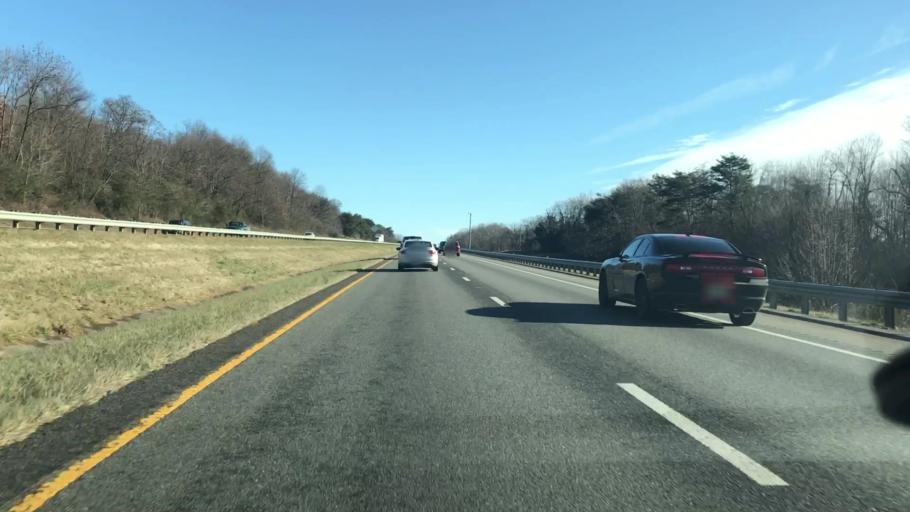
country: US
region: Virginia
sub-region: City of Salem
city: Salem
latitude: 37.2933
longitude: -80.0967
